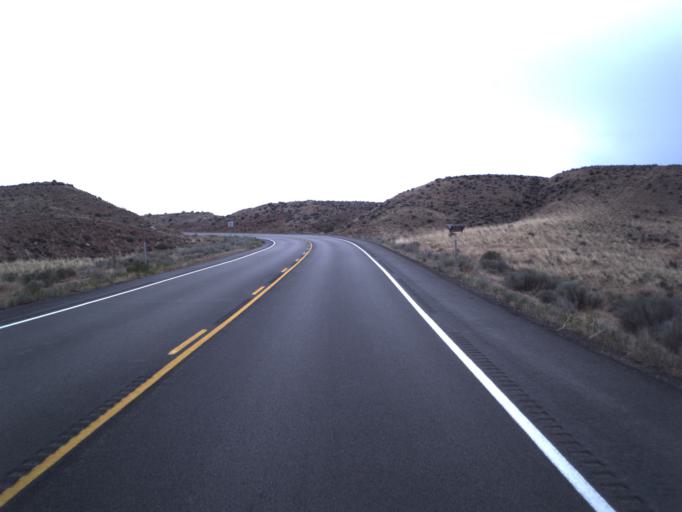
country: US
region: Utah
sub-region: Uintah County
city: Naples
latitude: 40.3057
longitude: -109.4801
